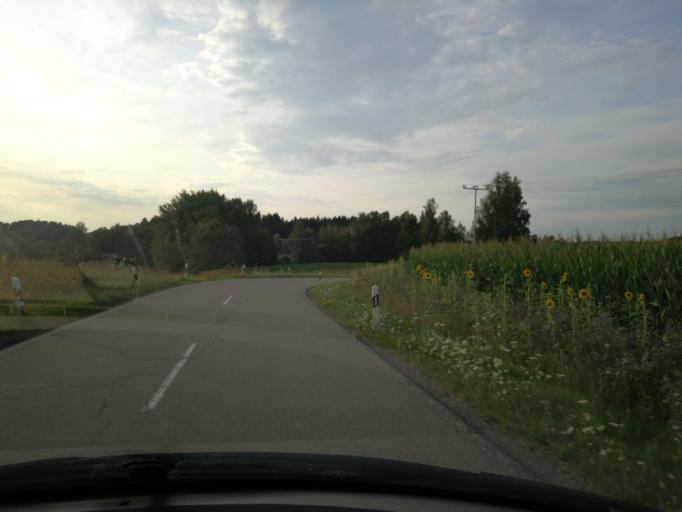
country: DE
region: Bavaria
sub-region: Lower Bavaria
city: Wiesenfelden
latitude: 49.0515
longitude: 12.5216
